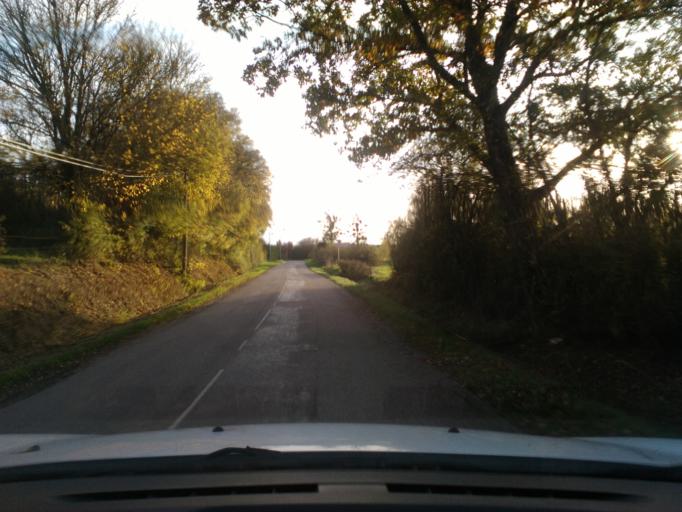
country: FR
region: Lorraine
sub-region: Departement des Vosges
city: Mirecourt
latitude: 48.2406
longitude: 6.1529
